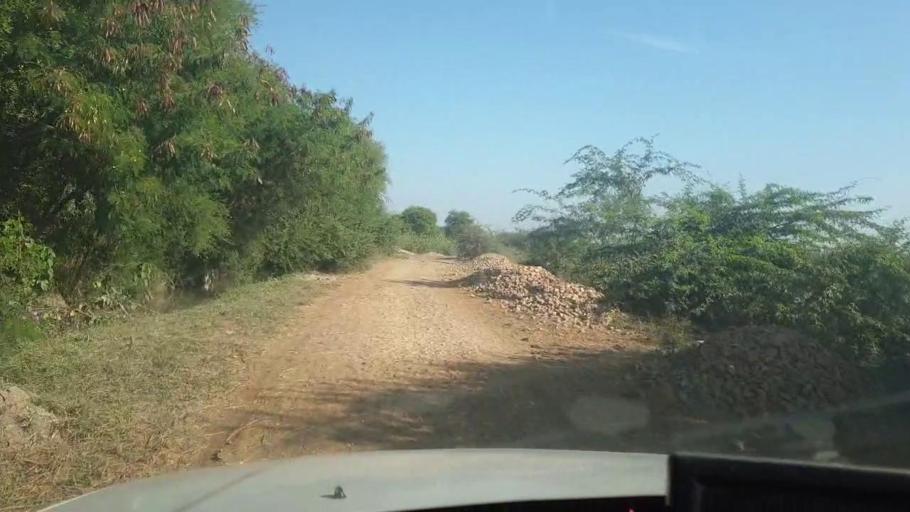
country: PK
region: Sindh
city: Mirpur Sakro
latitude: 24.4985
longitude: 67.6240
